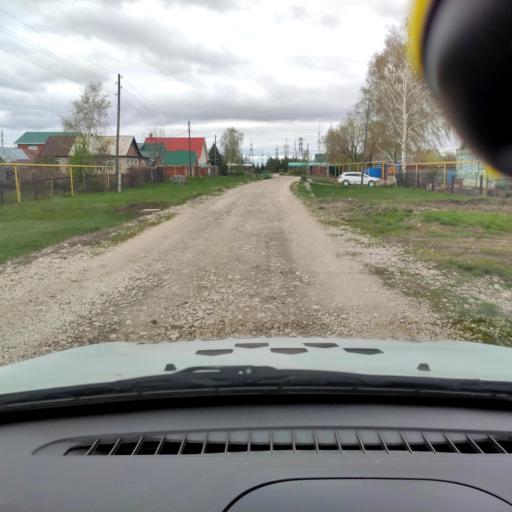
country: RU
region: Samara
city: Tol'yatti
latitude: 53.5830
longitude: 49.3304
